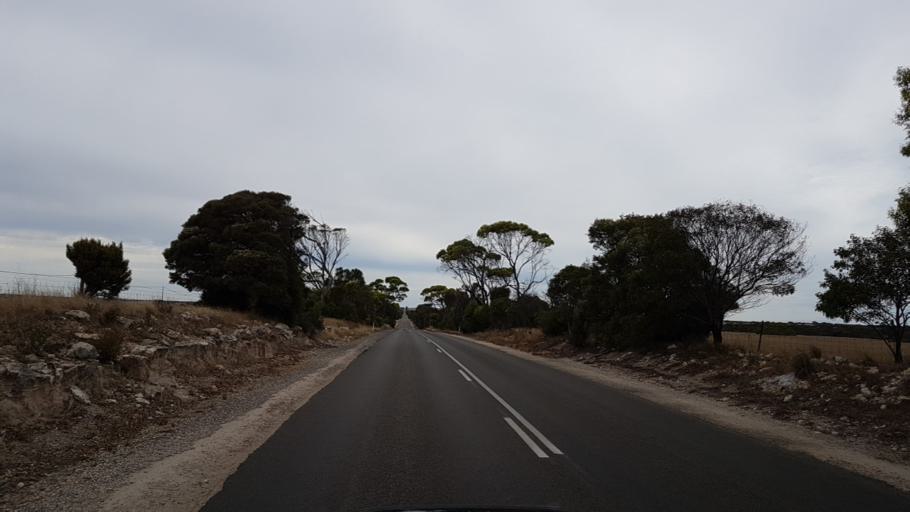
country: AU
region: South Australia
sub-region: Yorke Peninsula
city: Honiton
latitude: -34.9850
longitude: 137.2053
